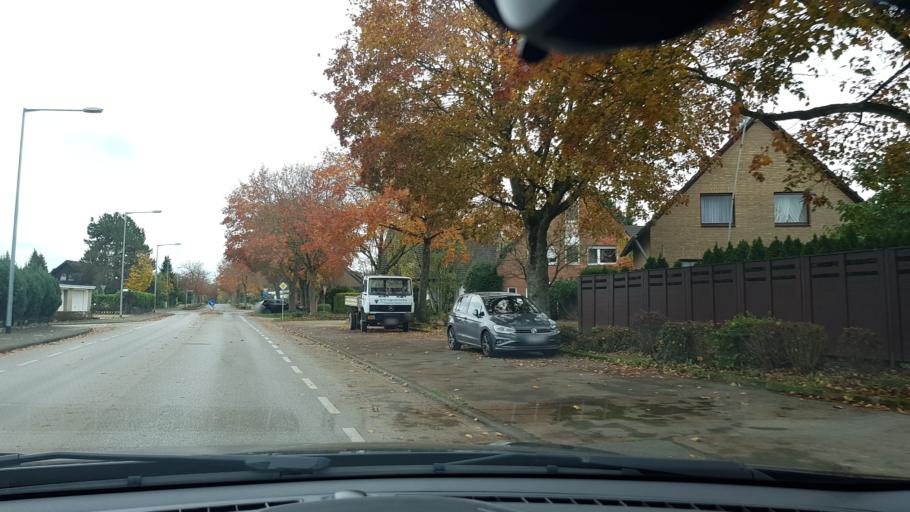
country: DE
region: North Rhine-Westphalia
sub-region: Regierungsbezirk Koln
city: Bedburg
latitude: 51.0008
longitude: 6.5546
